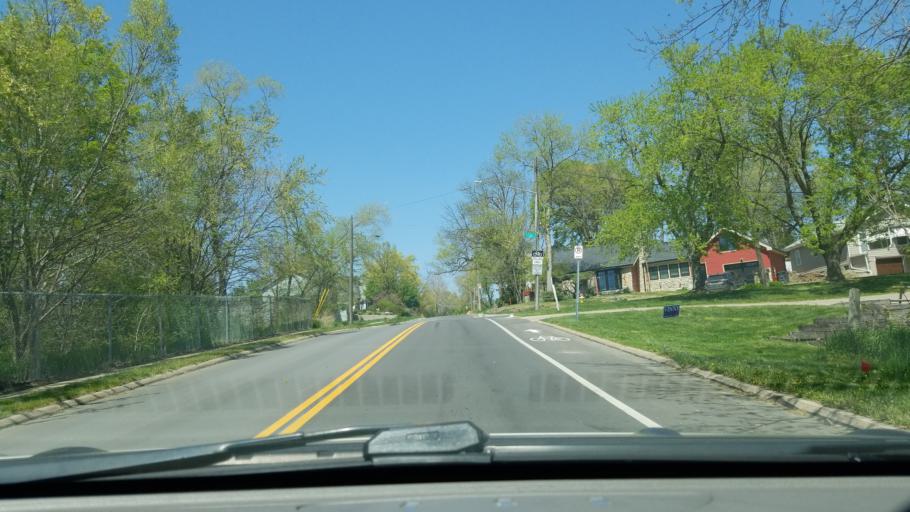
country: US
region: Nebraska
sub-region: Douglas County
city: Omaha
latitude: 41.2229
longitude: -95.9374
